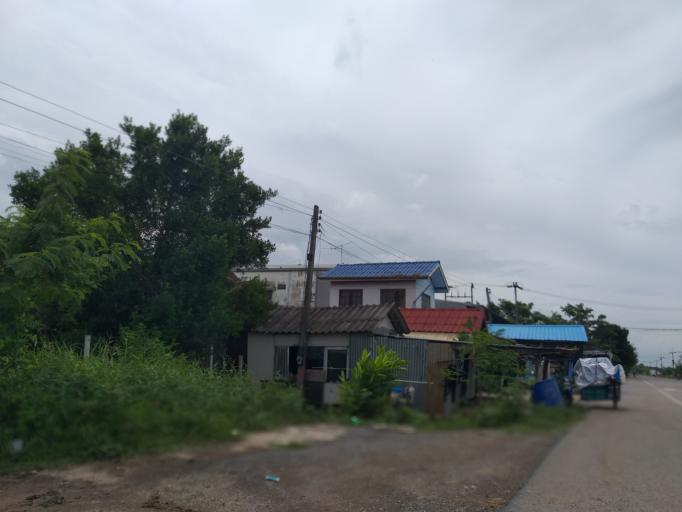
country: TH
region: Pathum Thani
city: Nong Suea
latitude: 14.0496
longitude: 100.8706
